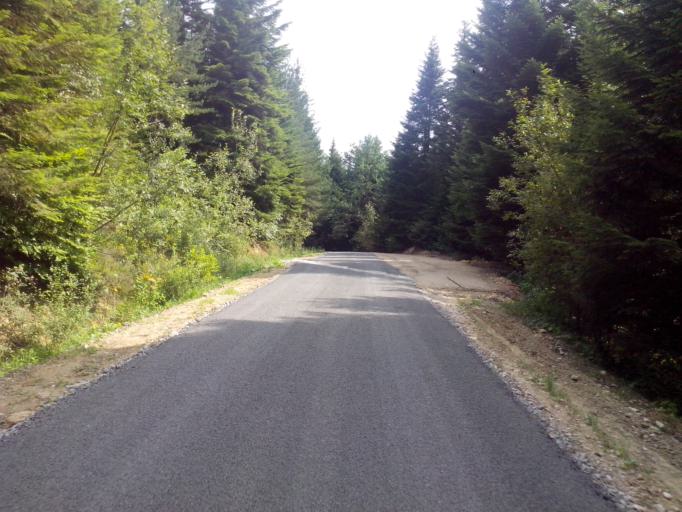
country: PL
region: Subcarpathian Voivodeship
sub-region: Powiat strzyzowski
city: Strzyzow
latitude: 49.8106
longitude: 21.8018
